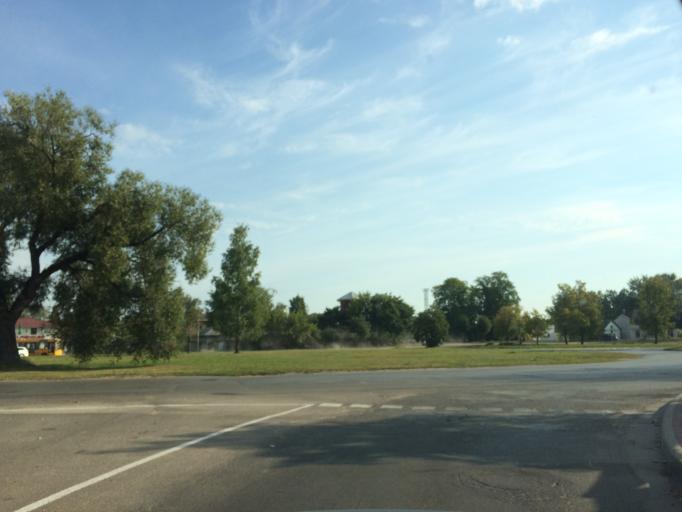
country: LV
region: Rezekne
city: Rezekne
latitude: 56.5181
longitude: 27.3455
